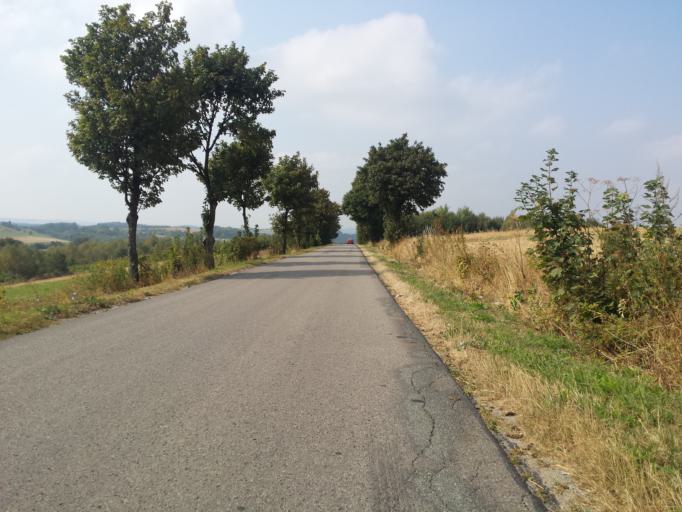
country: PL
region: Subcarpathian Voivodeship
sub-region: Powiat brzozowski
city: Wesola
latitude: 49.8416
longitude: 22.1503
